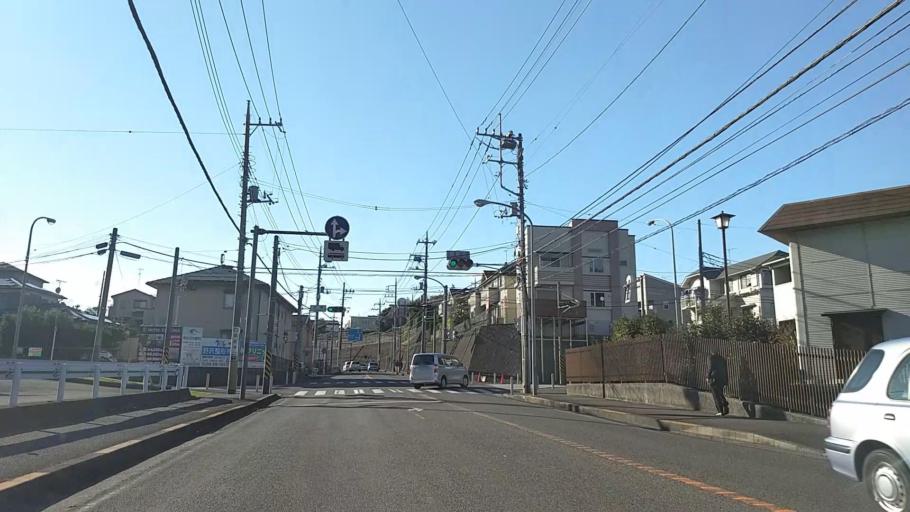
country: JP
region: Tokyo
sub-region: Machida-shi
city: Machida
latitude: 35.5198
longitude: 139.5578
